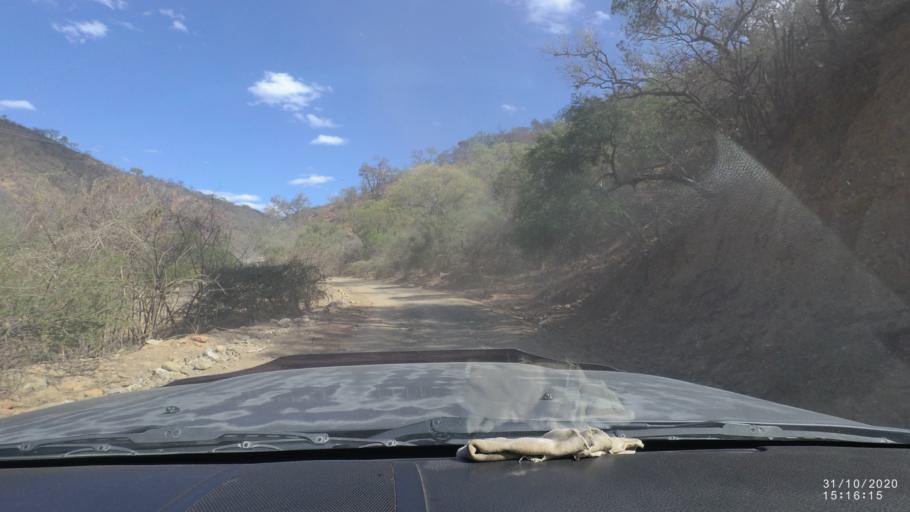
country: BO
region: Cochabamba
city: Aiquile
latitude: -18.3343
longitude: -64.7729
